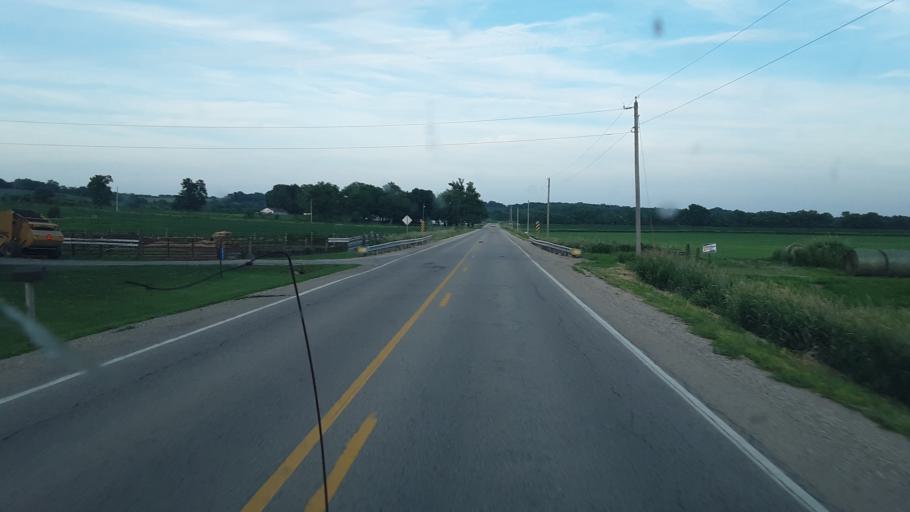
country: US
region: Iowa
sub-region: Benton County
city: Belle Plaine
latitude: 41.9195
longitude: -92.3696
